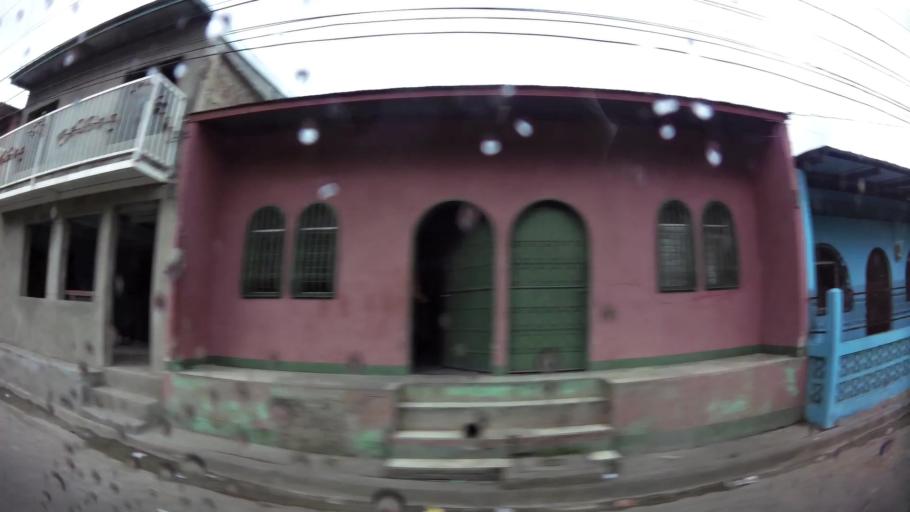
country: NI
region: Jinotega
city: Jinotega
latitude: 13.1001
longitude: -86.0031
